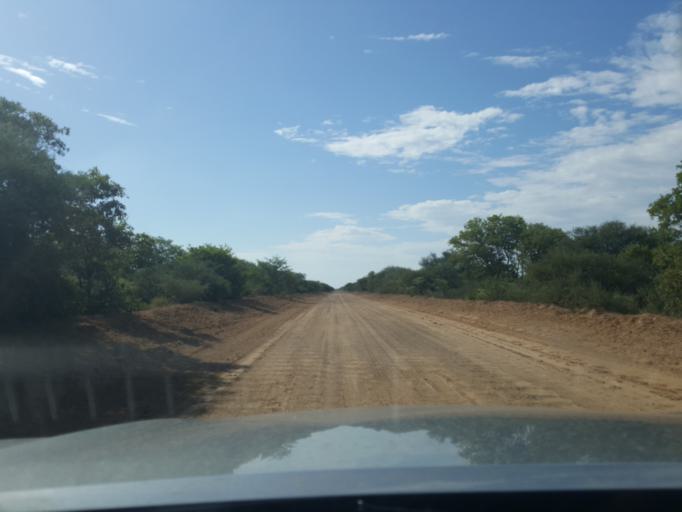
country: BW
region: Kweneng
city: Khudumelapye
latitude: -23.5097
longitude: 24.7120
